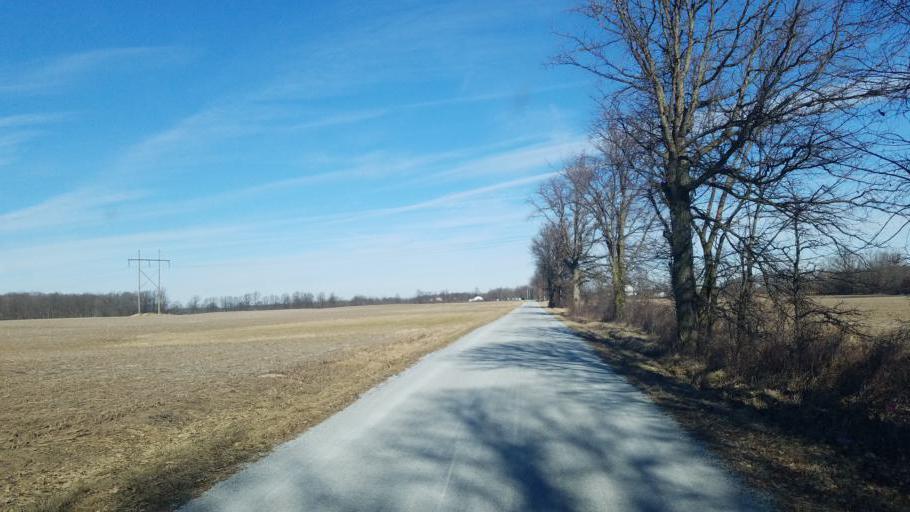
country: US
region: Ohio
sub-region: Union County
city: Richwood
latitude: 40.5737
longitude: -83.4189
